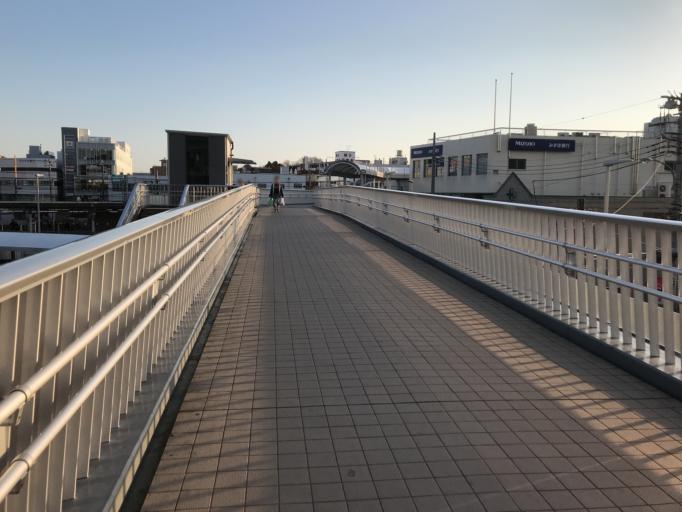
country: JP
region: Tokyo
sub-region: Machida-shi
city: Machida
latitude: 35.5326
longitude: 139.4957
